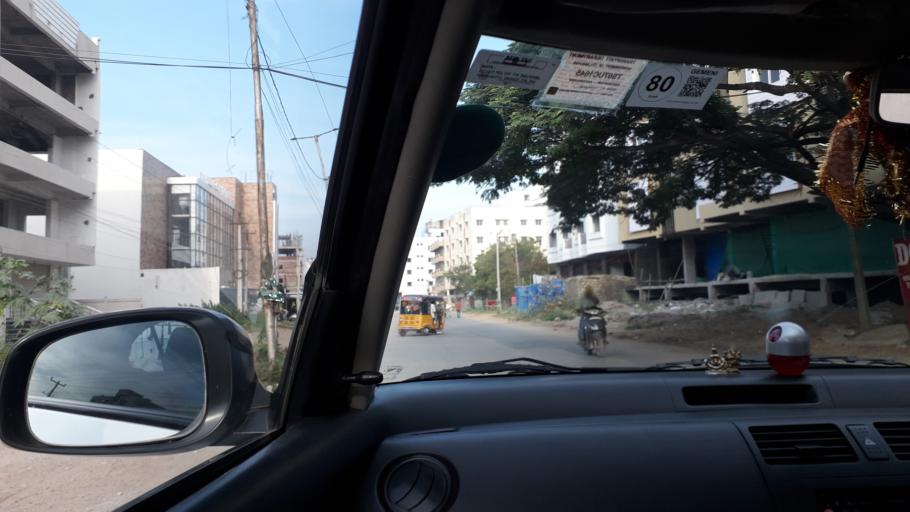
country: IN
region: Telangana
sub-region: Hyderabad
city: Hyderabad
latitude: 17.3941
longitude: 78.3859
